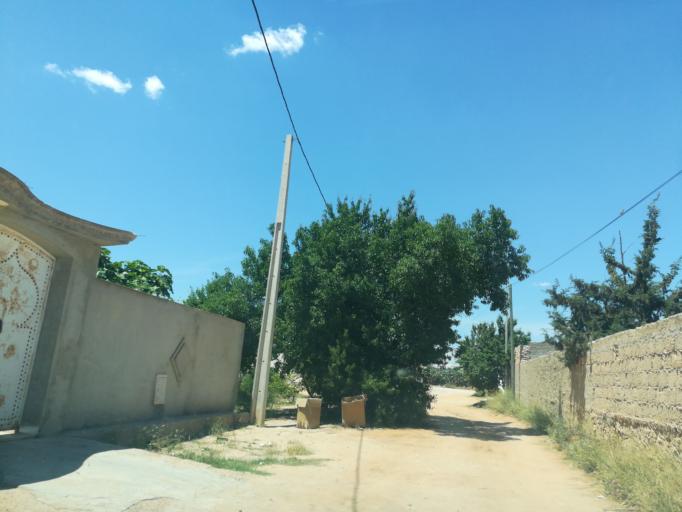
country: TN
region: Safaqis
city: Al Qarmadah
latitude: 34.8159
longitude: 10.7597
